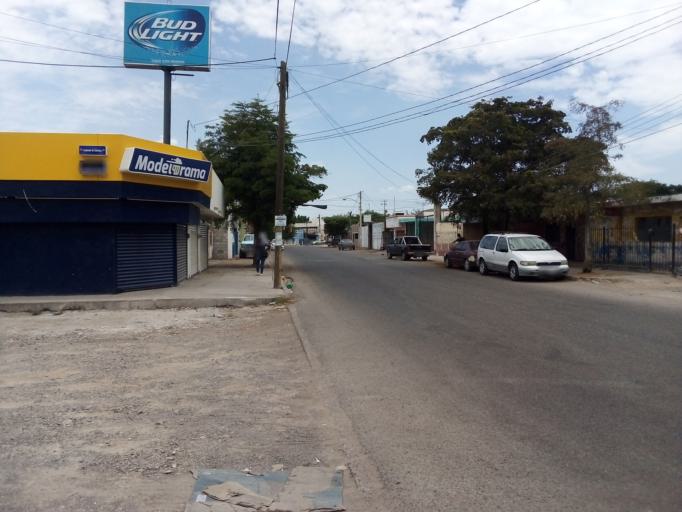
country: MX
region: Sinaloa
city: Culiacan
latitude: 24.7707
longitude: -107.4303
